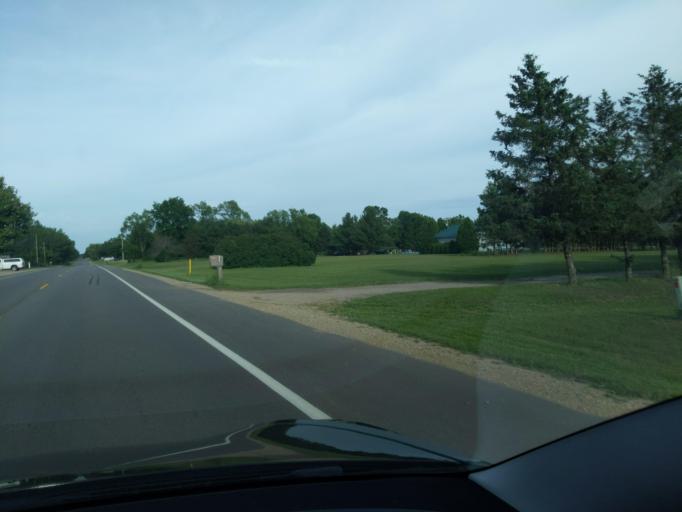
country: US
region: Michigan
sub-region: Montcalm County
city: Howard City
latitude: 43.3957
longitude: -85.5001
